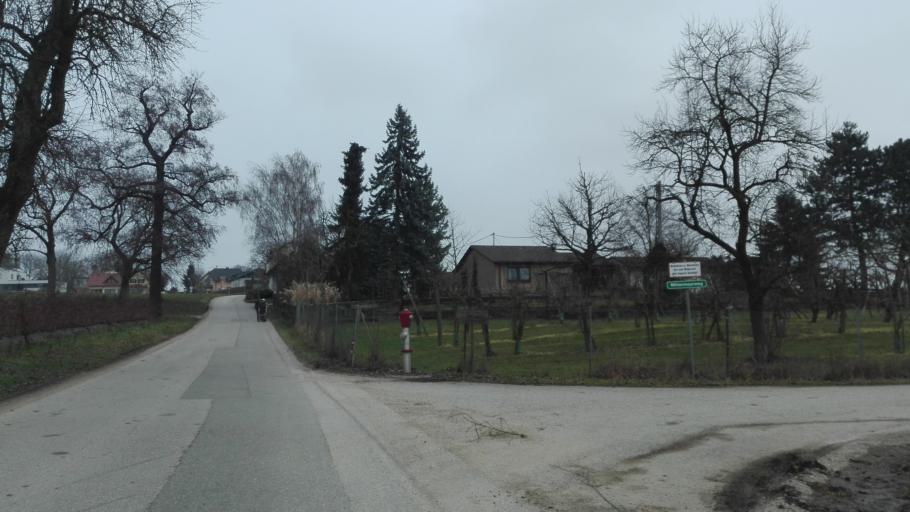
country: AT
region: Upper Austria
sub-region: Politischer Bezirk Linz-Land
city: Horsching
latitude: 48.2470
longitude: 14.1480
